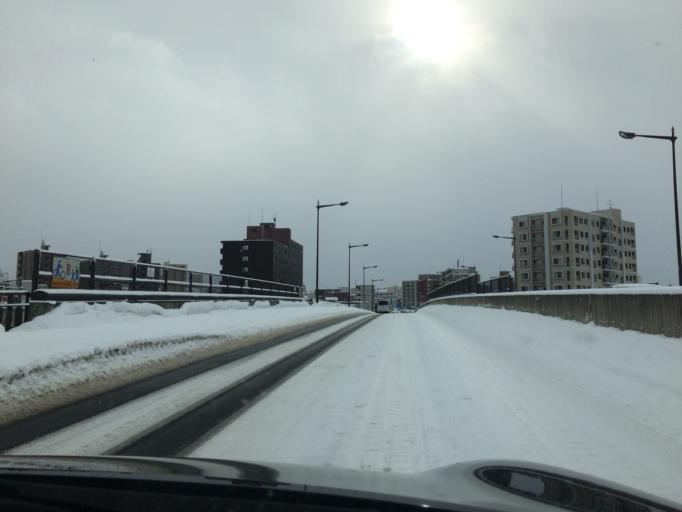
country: JP
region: Hokkaido
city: Ebetsu
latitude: 43.0478
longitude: 141.4703
